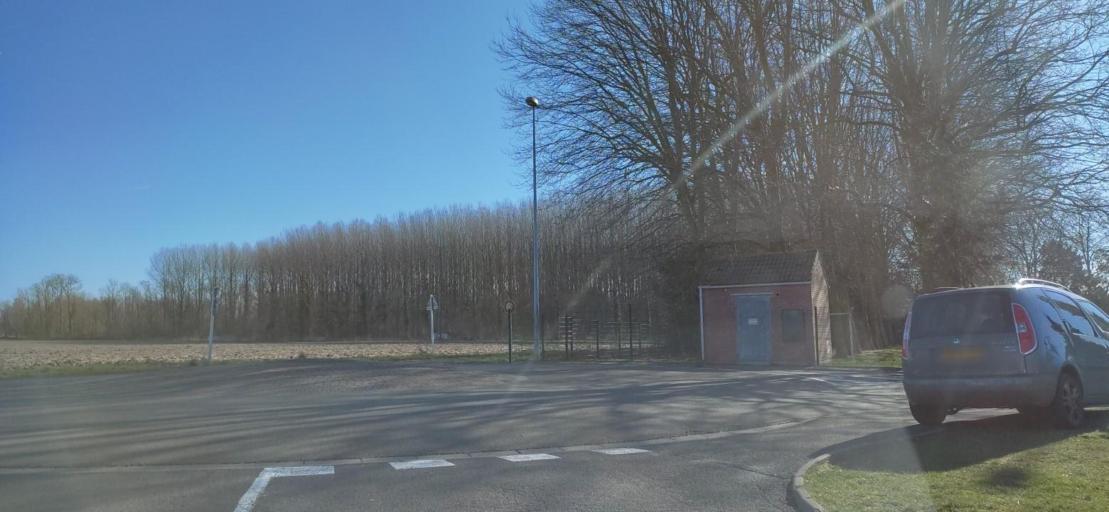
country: FR
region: Nord-Pas-de-Calais
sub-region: Departement du Nord
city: Camphin-en-Carembault
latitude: 50.4973
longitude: 2.9778
